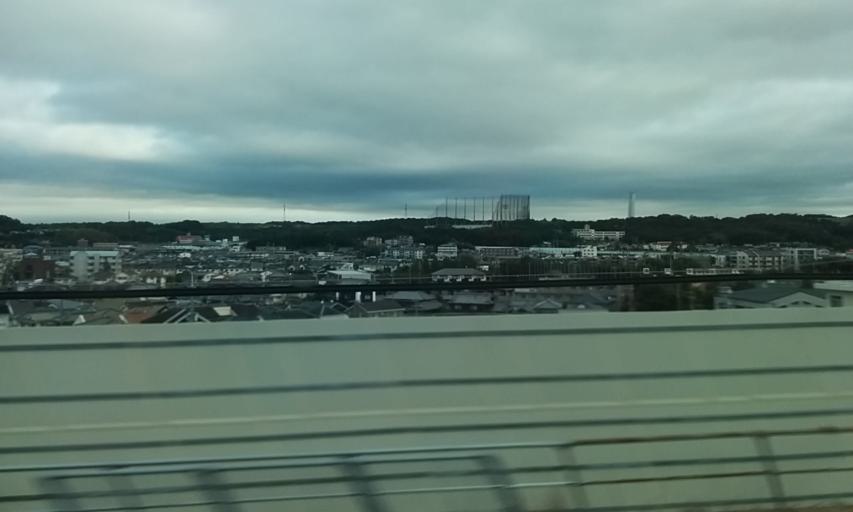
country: JP
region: Hyogo
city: Akashi
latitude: 34.6683
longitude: 135.0177
